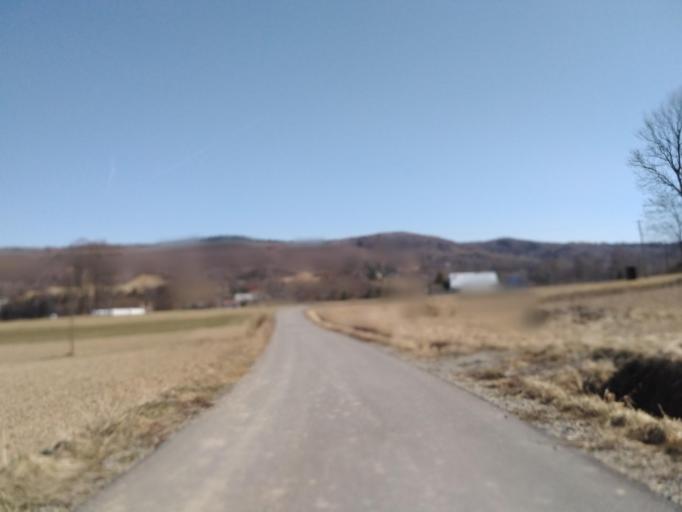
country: PL
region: Subcarpathian Voivodeship
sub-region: Powiat brzozowski
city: Jasienica Rosielna
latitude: 49.7634
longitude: 21.9493
